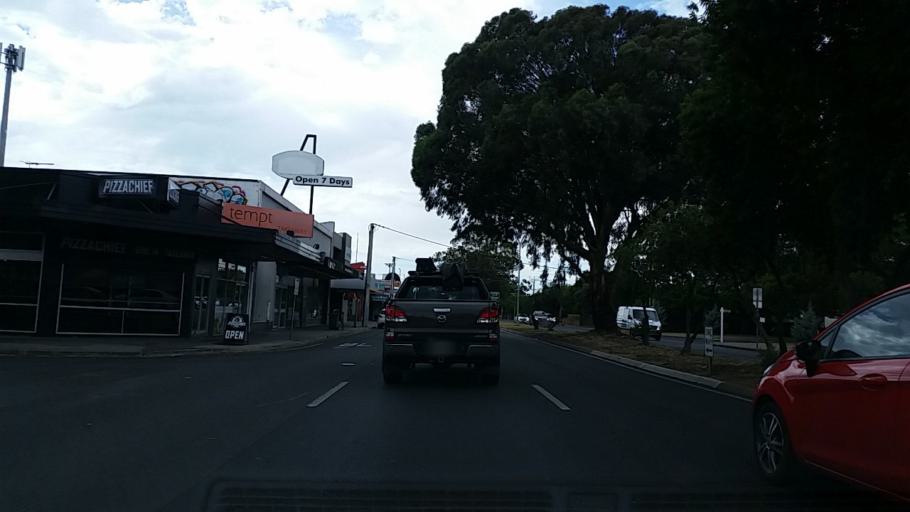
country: AU
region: South Australia
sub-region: Mitcham
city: Clarence Gardens
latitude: -34.9807
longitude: 138.5919
